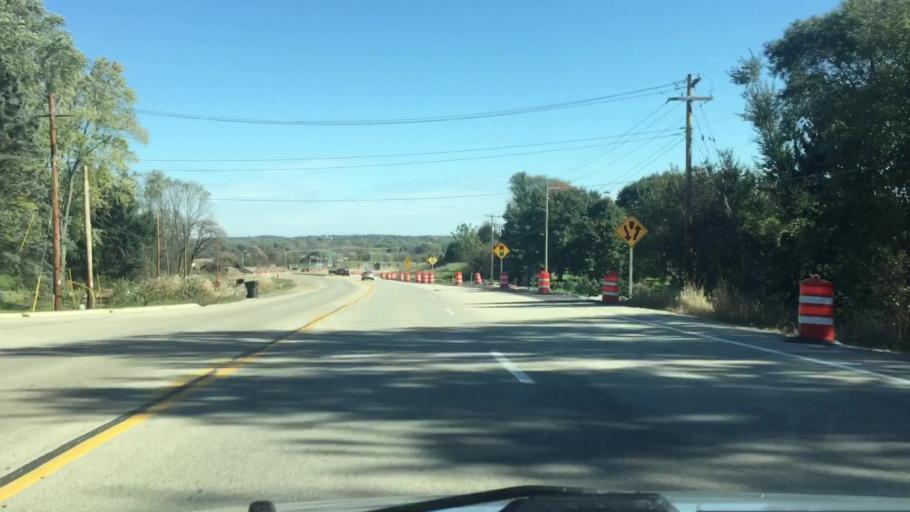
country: US
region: Wisconsin
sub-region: Waukesha County
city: Waukesha
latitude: 42.9785
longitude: -88.2795
